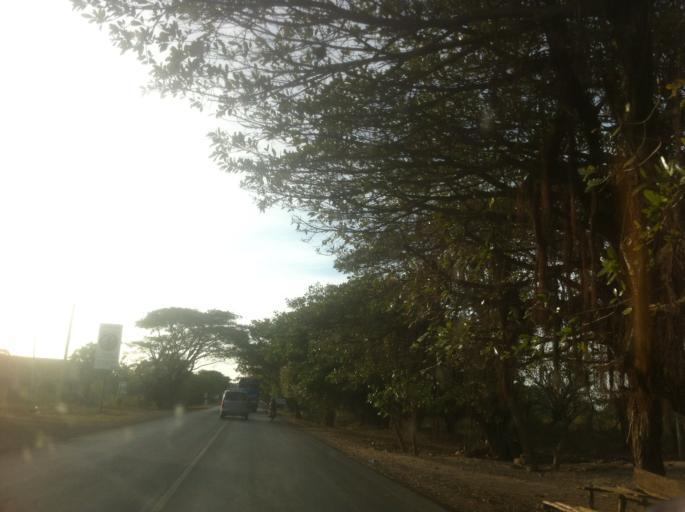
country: NI
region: Rivas
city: Rivas
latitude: 11.4467
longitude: -85.8297
